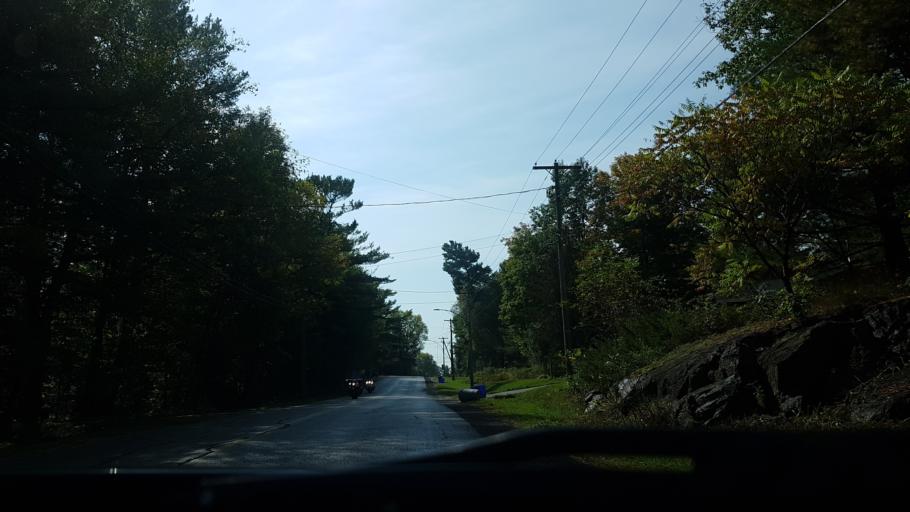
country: CA
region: Ontario
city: Gravenhurst
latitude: 44.7564
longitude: -79.3328
